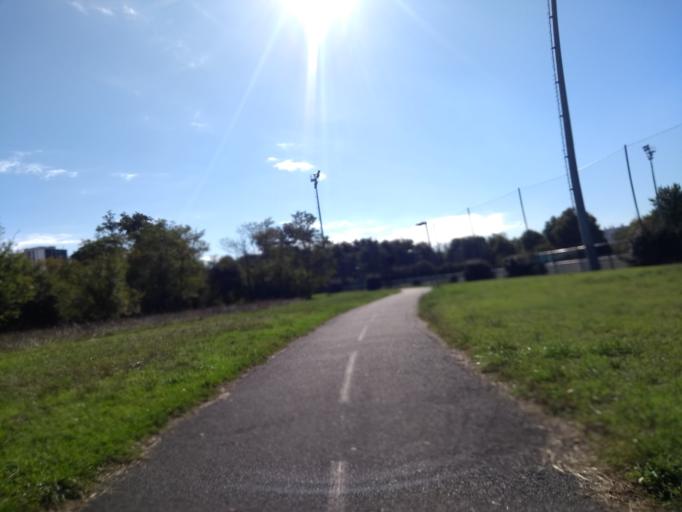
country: FR
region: Aquitaine
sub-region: Departement de la Gironde
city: Pessac
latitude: 44.7935
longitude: -0.6348
